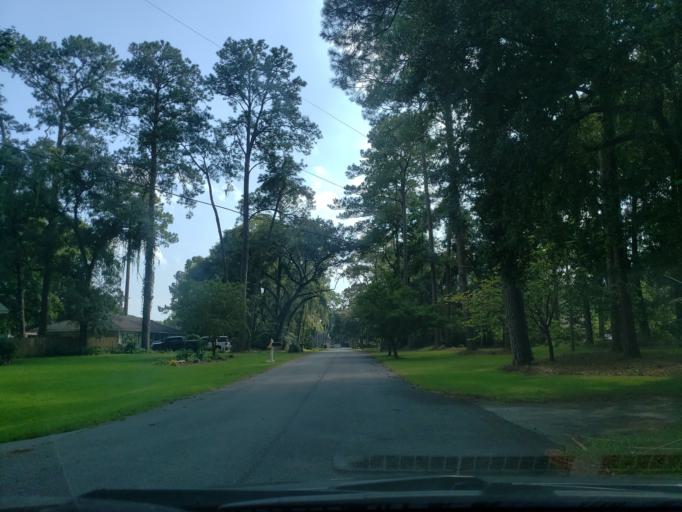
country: US
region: Georgia
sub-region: Chatham County
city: Montgomery
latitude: 31.9302
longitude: -81.0959
